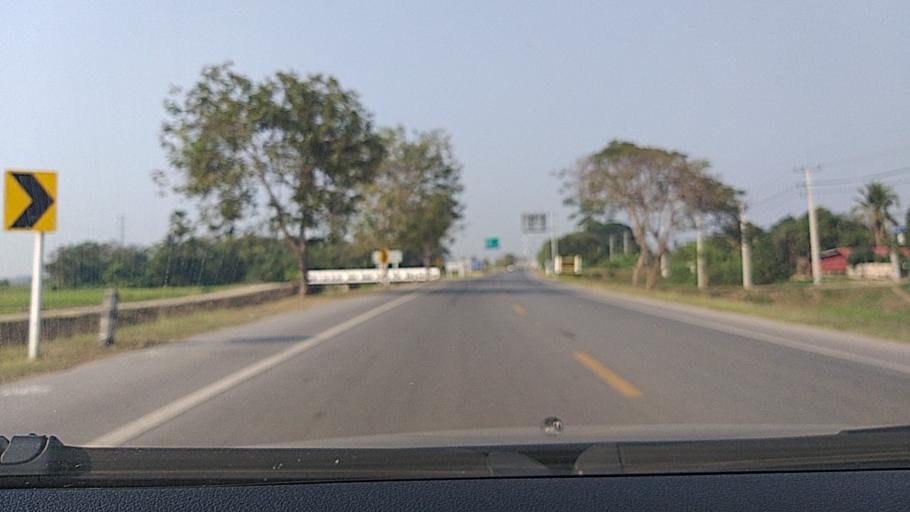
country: TH
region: Sing Buri
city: Tha Chang
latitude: 14.7260
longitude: 100.4300
